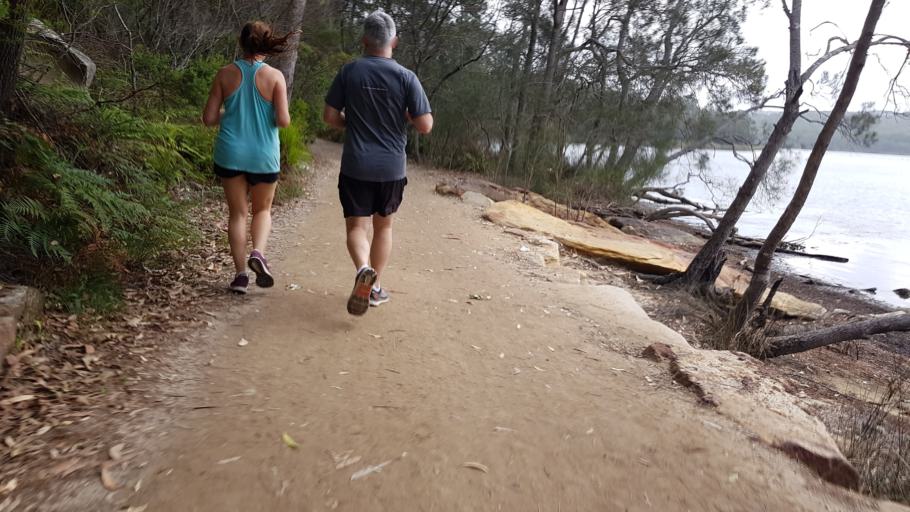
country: AU
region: New South Wales
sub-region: Pittwater
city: North Narrabeen
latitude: -33.7153
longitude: 151.2810
